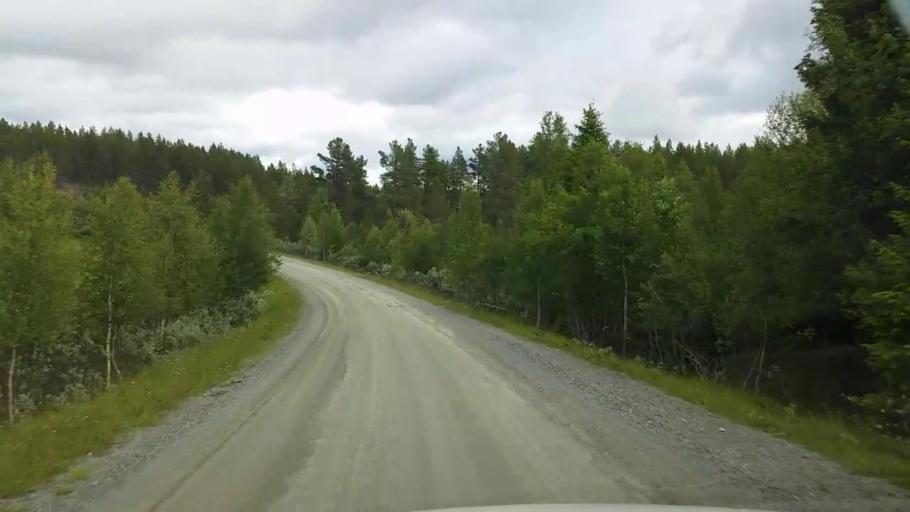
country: NO
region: Hedmark
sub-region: Engerdal
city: Engerdal
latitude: 62.3315
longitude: 12.6433
